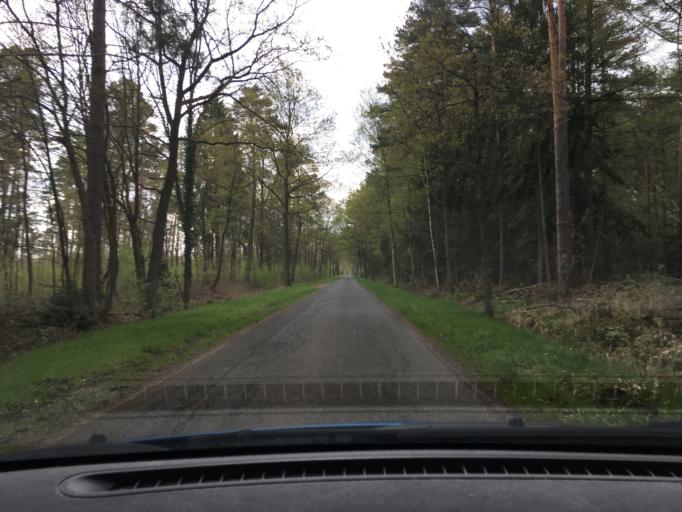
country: DE
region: Lower Saxony
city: Radbruch
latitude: 53.2856
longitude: 10.2608
